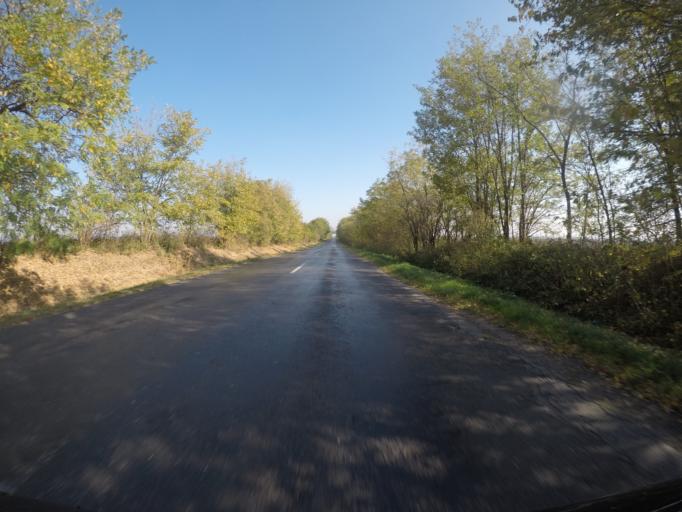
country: HU
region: Tolna
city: Dunaszentgyorgy
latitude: 46.6001
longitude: 18.7671
